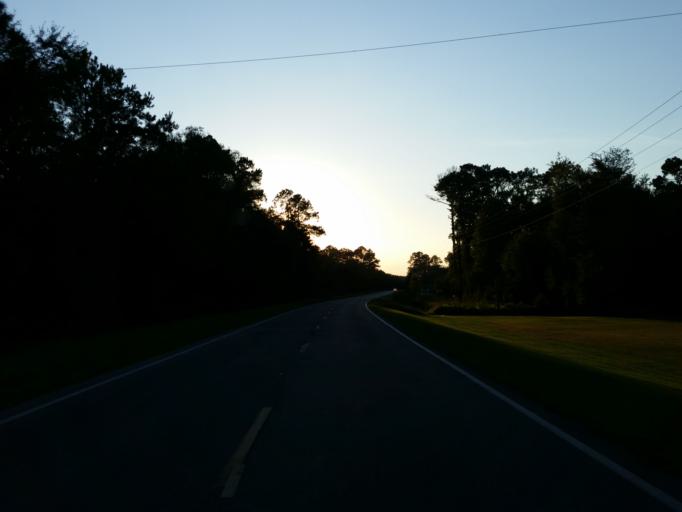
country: US
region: Georgia
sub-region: Berrien County
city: Nashville
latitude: 31.1963
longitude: -83.2194
